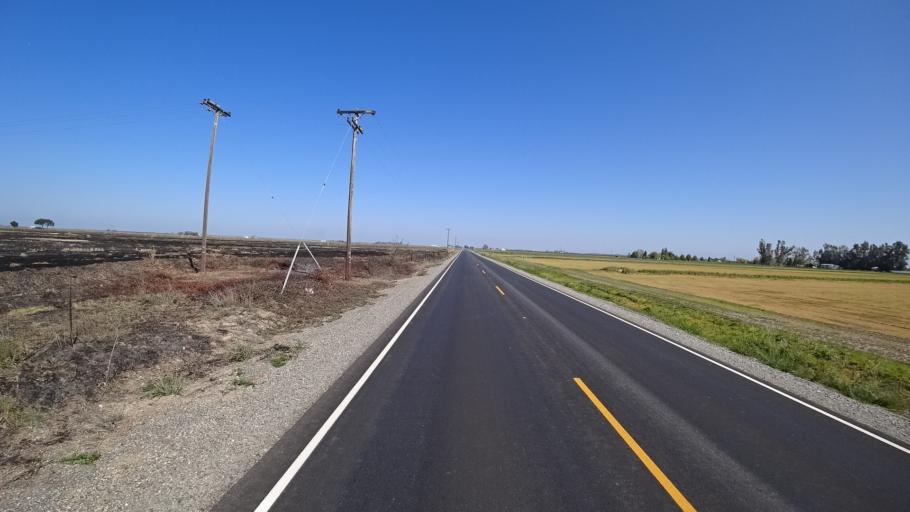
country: US
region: California
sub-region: Glenn County
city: Willows
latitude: 39.5982
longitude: -122.0648
